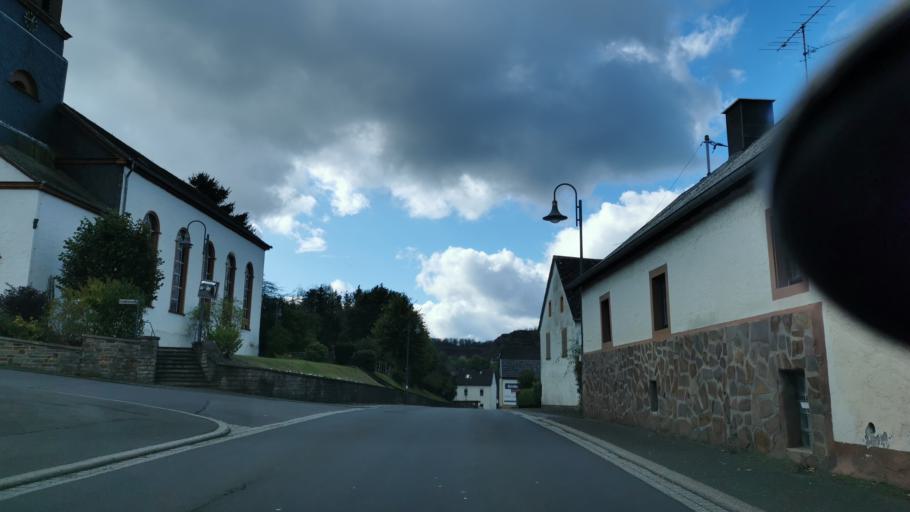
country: DE
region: Rheinland-Pfalz
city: Walsdorf
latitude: 50.2796
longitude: 6.7144
